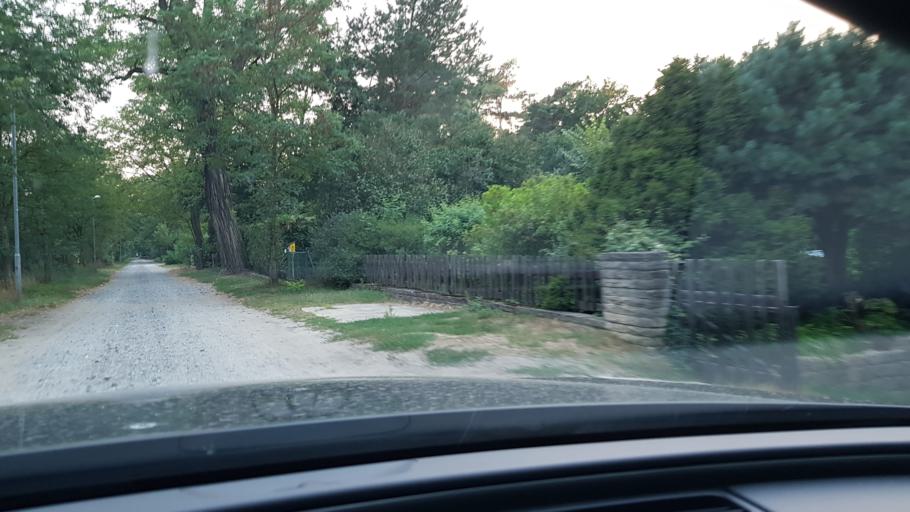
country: DE
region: Berlin
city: Friedrichshagen
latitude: 52.4782
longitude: 13.6279
